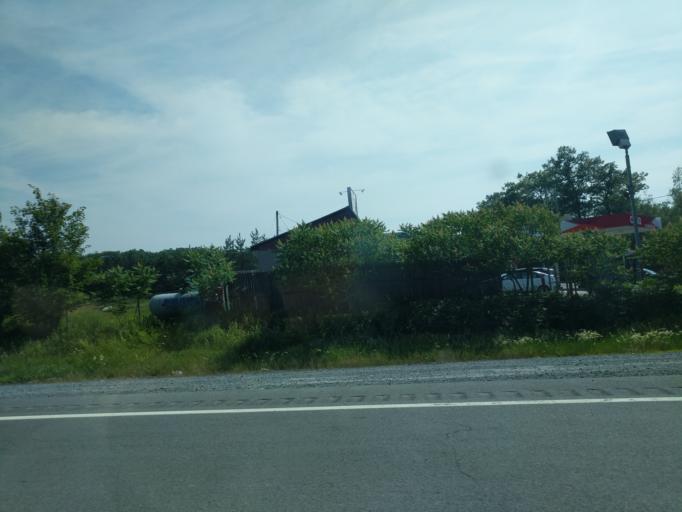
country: US
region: New York
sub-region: Sullivan County
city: Rock Hill
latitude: 41.6063
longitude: -74.5644
